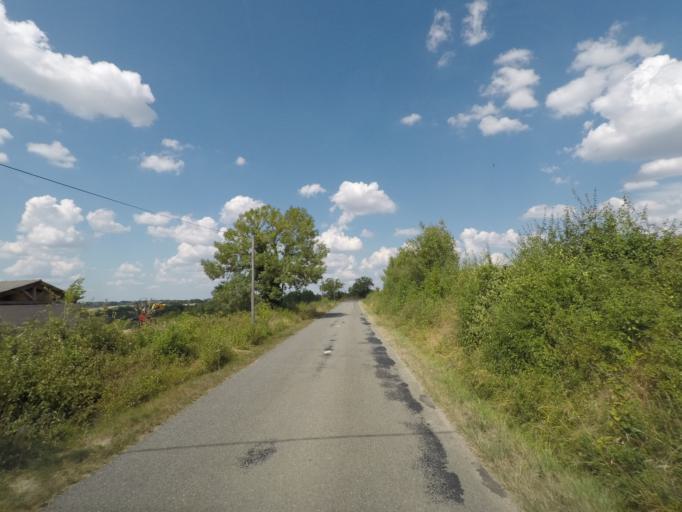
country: FR
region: Midi-Pyrenees
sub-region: Departement du Lot
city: Le Vigan
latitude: 44.6176
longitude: 1.5984
